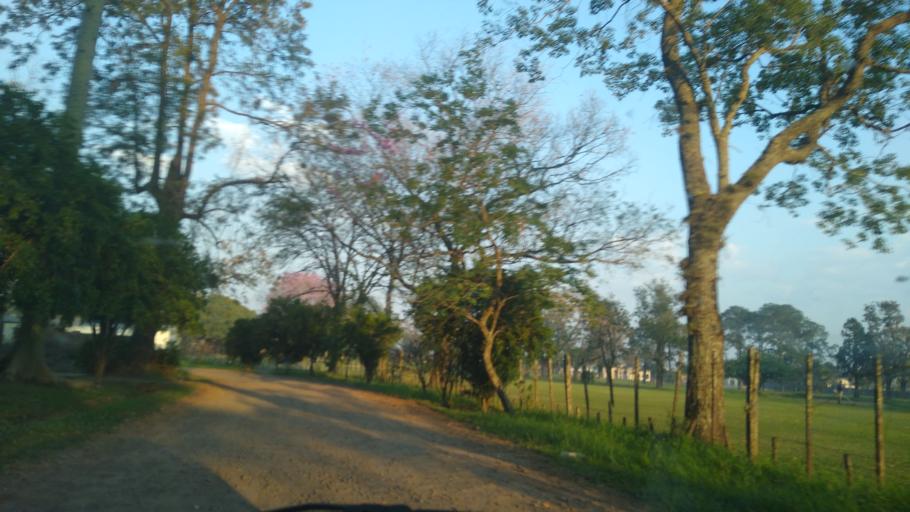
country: AR
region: Chaco
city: Barranqueras
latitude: -27.4662
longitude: -58.9559
